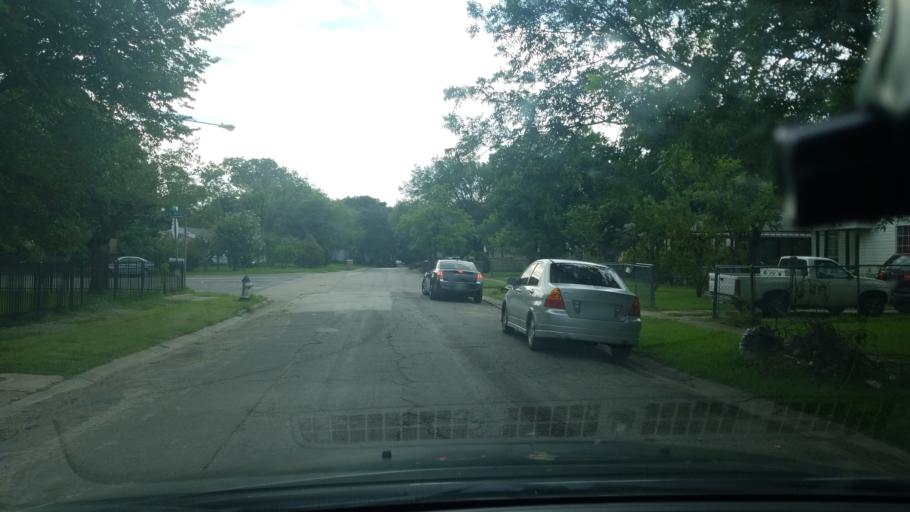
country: US
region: Texas
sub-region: Dallas County
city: Balch Springs
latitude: 32.7396
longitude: -96.6708
